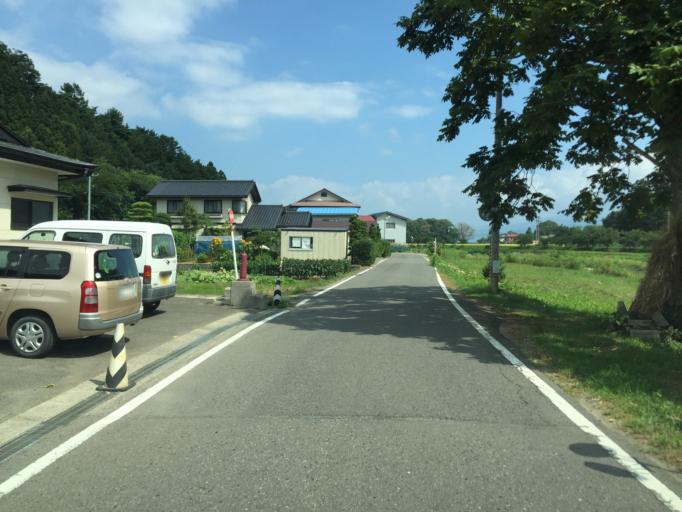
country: JP
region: Fukushima
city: Inawashiro
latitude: 37.4127
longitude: 140.1237
